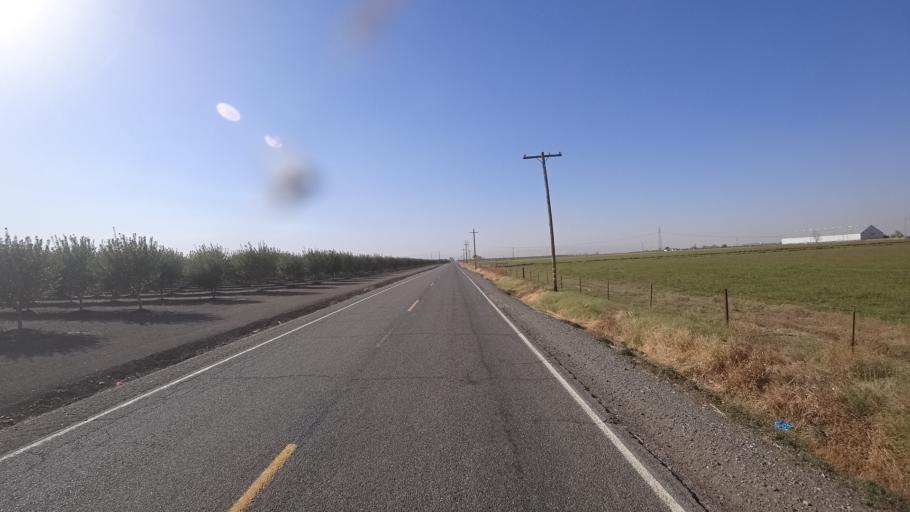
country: US
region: California
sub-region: Yolo County
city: Cottonwood
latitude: 38.7162
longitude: -121.9353
